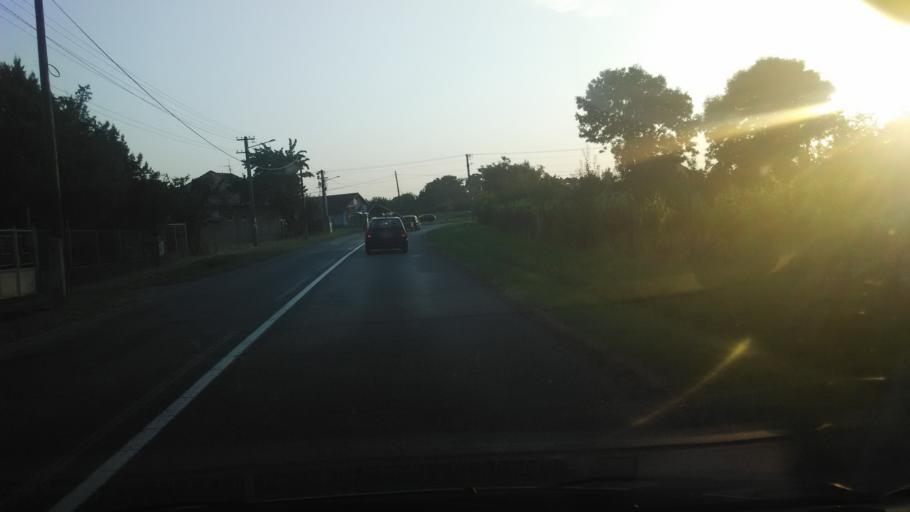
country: SK
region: Nitriansky
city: Tlmace
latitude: 48.1861
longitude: 18.4669
